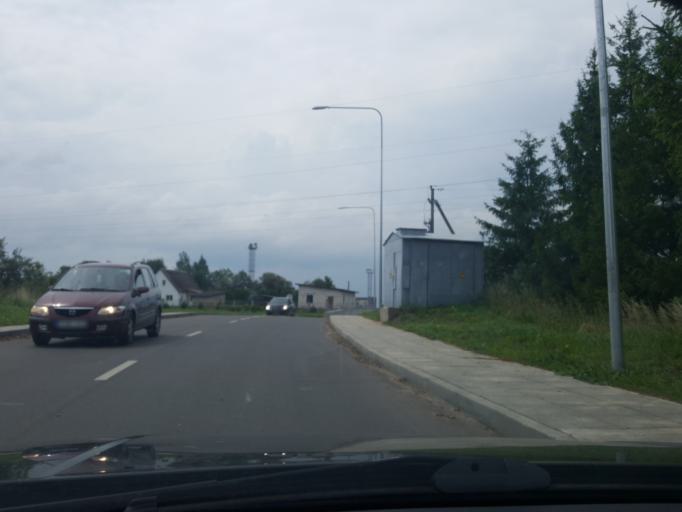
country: LT
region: Alytaus apskritis
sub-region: Alytus
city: Alytus
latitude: 54.4373
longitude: 24.0175
